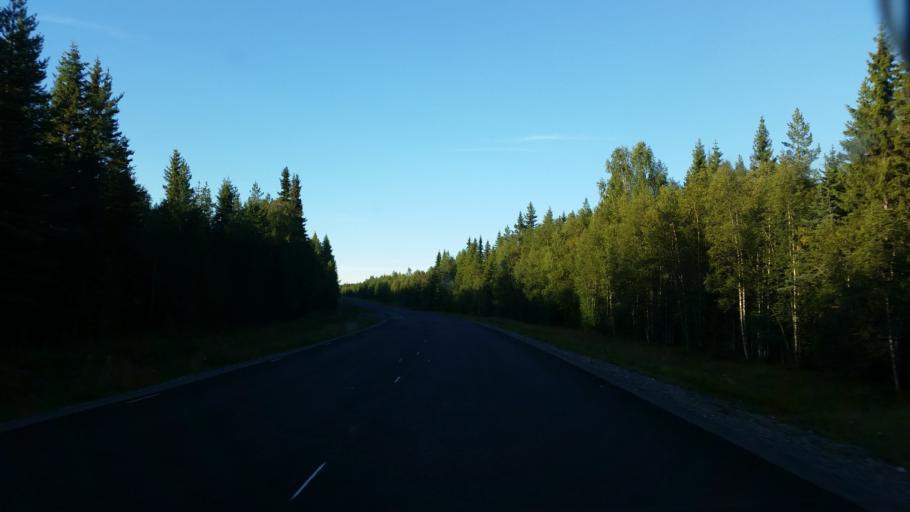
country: SE
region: Vaesterbotten
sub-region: Dorotea Kommun
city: Dorotea
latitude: 64.3042
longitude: 16.5912
